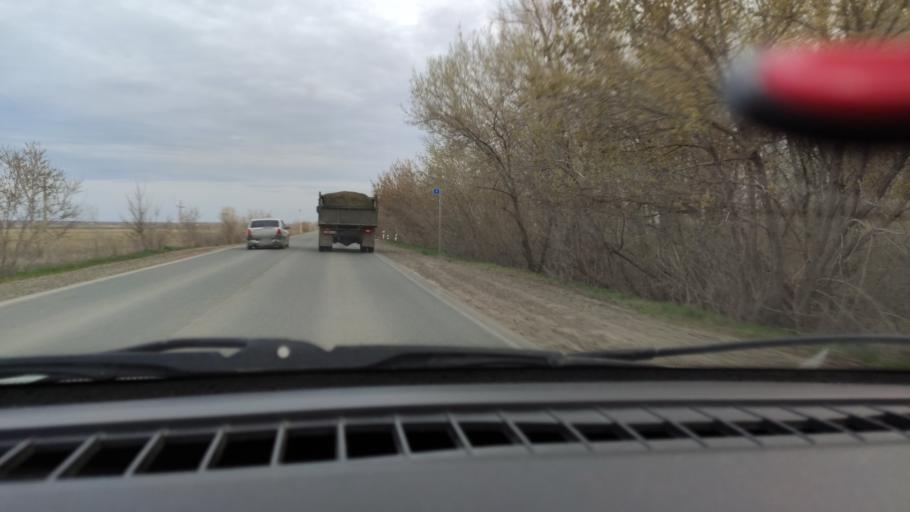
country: RU
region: Orenburg
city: Tatarskaya Kargala
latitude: 51.9278
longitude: 55.1737
